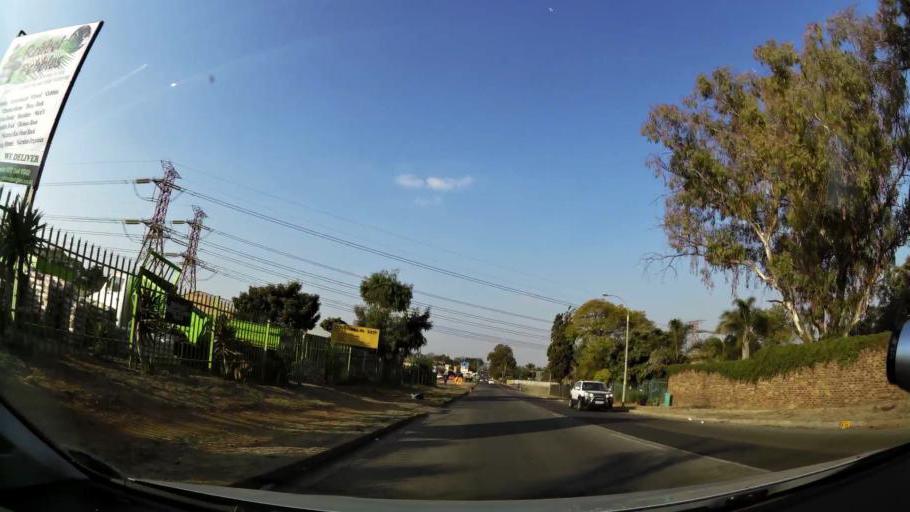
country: ZA
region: Gauteng
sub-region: City of Johannesburg Metropolitan Municipality
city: Modderfontein
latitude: -26.0709
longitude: 28.2166
